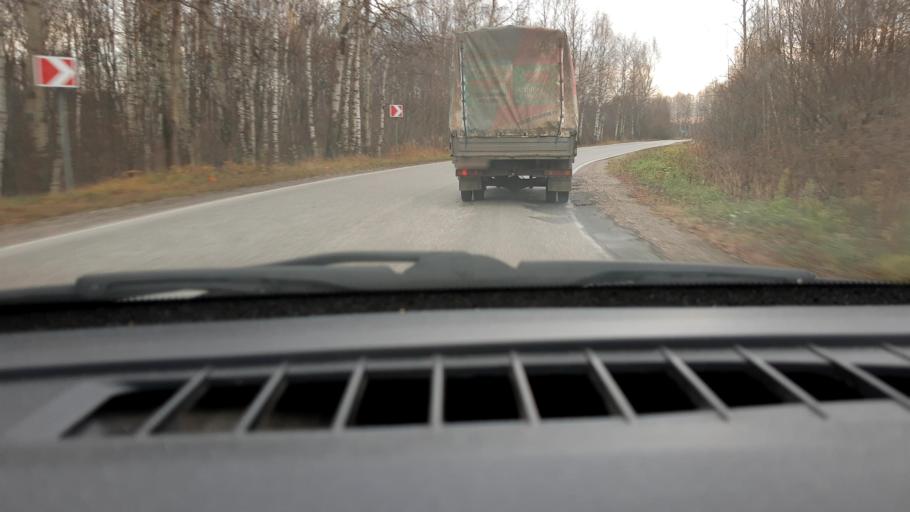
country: RU
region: Nizjnij Novgorod
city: Neklyudovo
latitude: 56.4979
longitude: 43.8534
